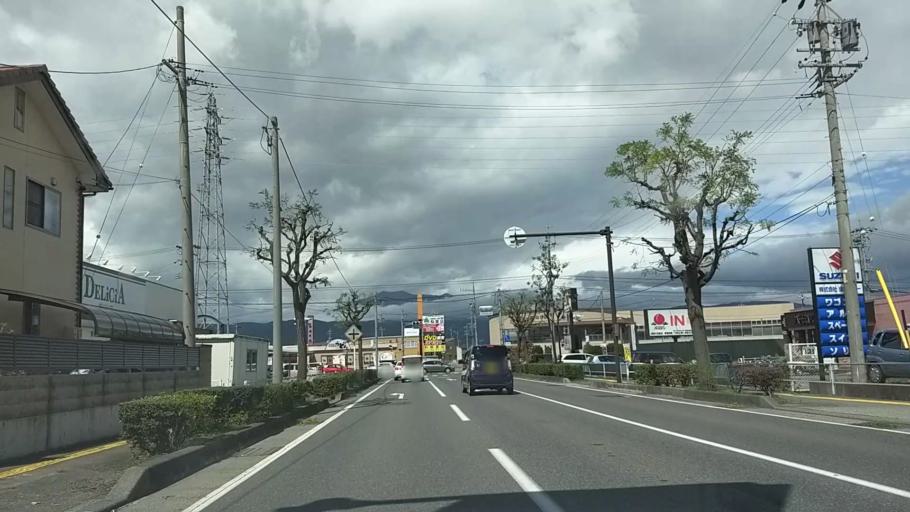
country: JP
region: Nagano
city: Nagano-shi
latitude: 36.6269
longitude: 138.2365
